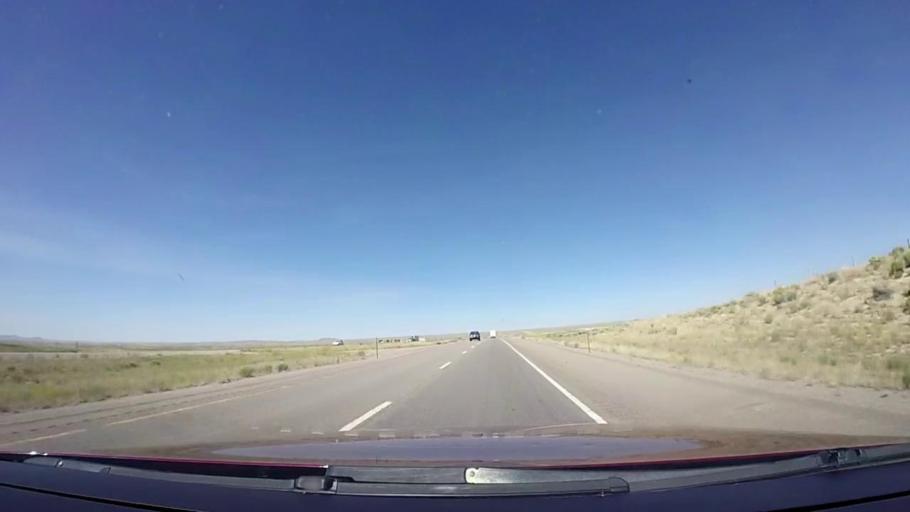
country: US
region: Wyoming
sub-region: Sweetwater County
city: Rock Springs
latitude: 41.6394
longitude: -108.4720
